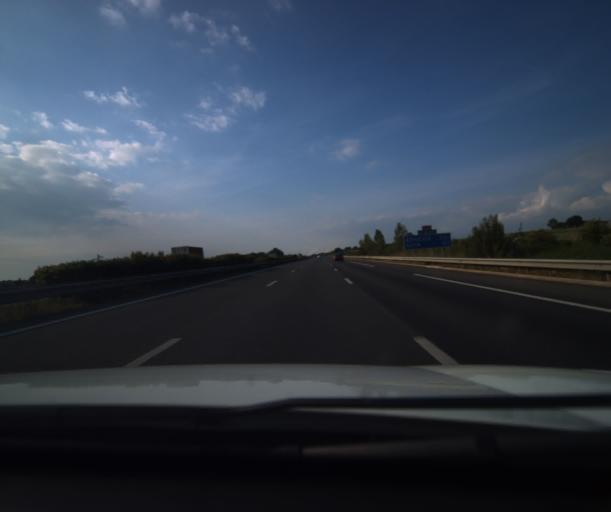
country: FR
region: Midi-Pyrenees
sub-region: Departement de la Haute-Garonne
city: Bouloc
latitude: 43.7774
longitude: 1.3835
